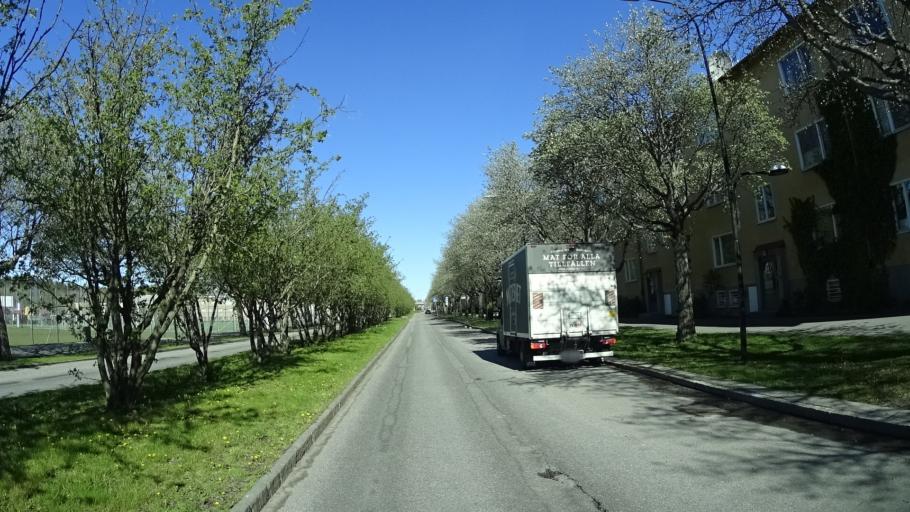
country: SE
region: Stockholm
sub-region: Stockholms Kommun
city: Arsta
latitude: 59.2821
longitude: 18.0769
